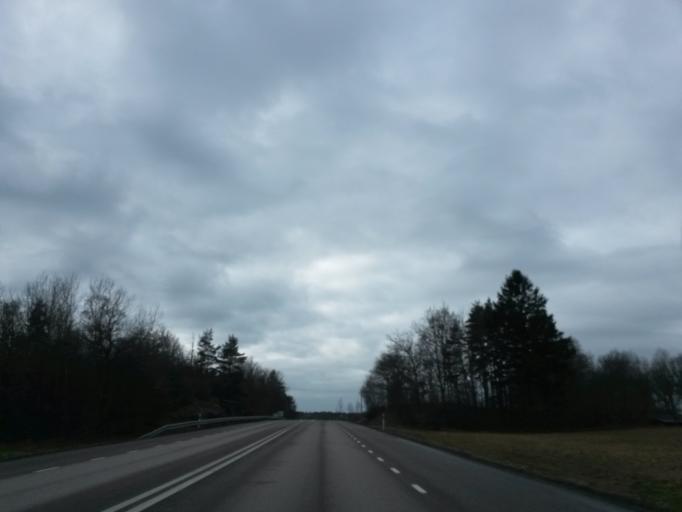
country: SE
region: Vaestra Goetaland
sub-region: Vargarda Kommun
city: Jonstorp
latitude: 58.0023
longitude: 12.7275
